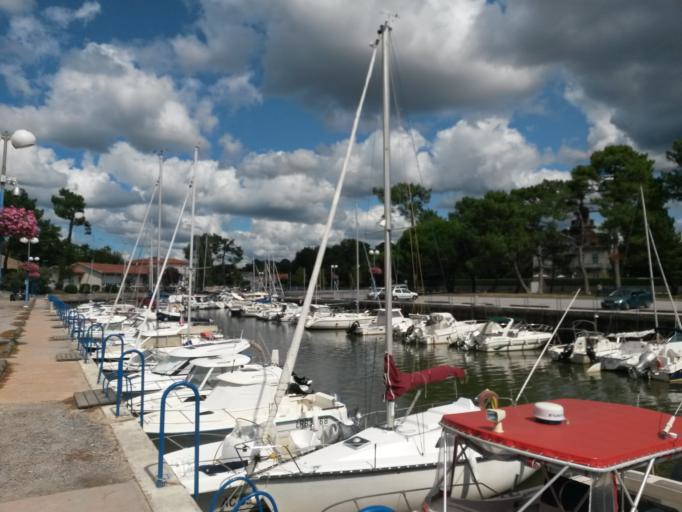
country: FR
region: Aquitaine
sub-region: Departement de la Gironde
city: Andernos-les-Bains
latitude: 44.7346
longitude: -1.0936
